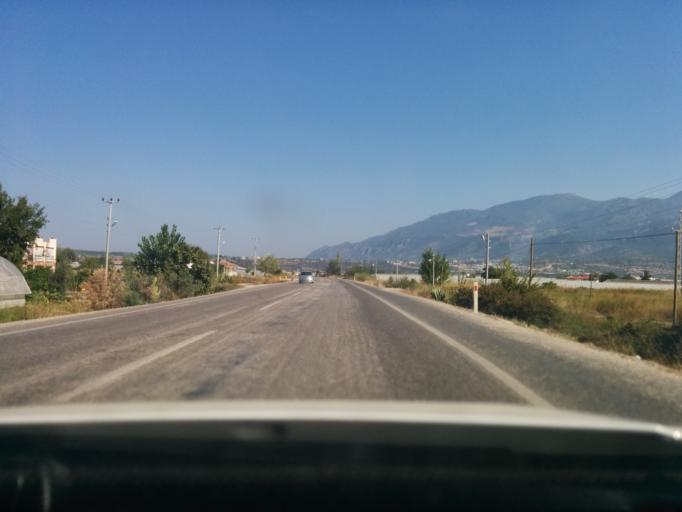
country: TR
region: Antalya
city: Kalkan
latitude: 36.3300
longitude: 29.3331
